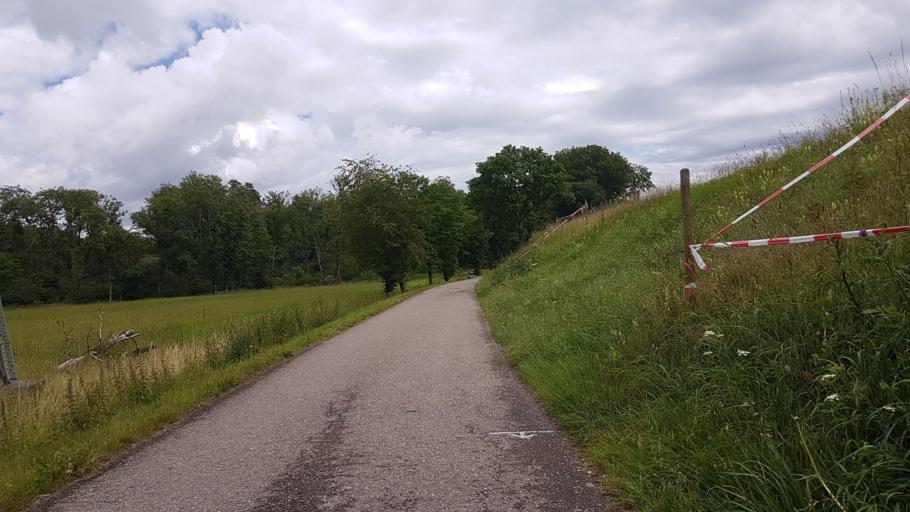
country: DE
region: Baden-Wuerttemberg
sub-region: Tuebingen Region
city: Erbach
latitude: 48.3160
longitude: 9.8773
